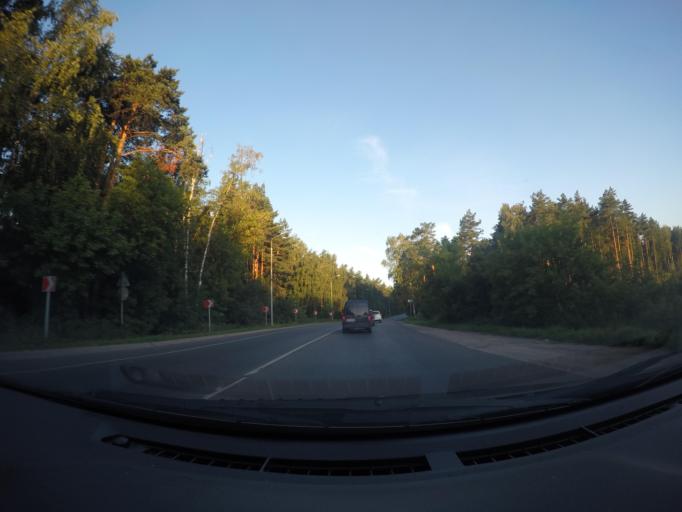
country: RU
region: Moskovskaya
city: Rodniki
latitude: 55.6562
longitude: 38.0515
